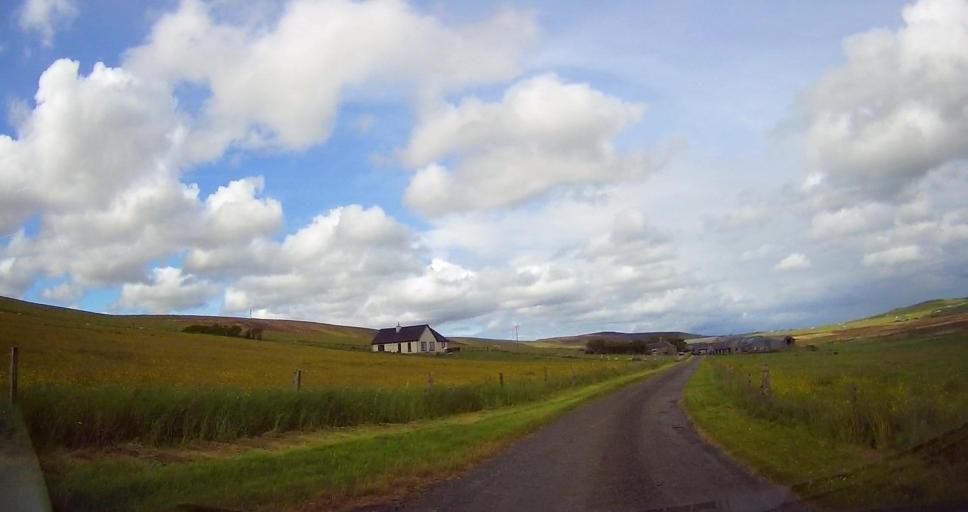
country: GB
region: Scotland
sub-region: Orkney Islands
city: Orkney
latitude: 59.0550
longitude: -3.1033
